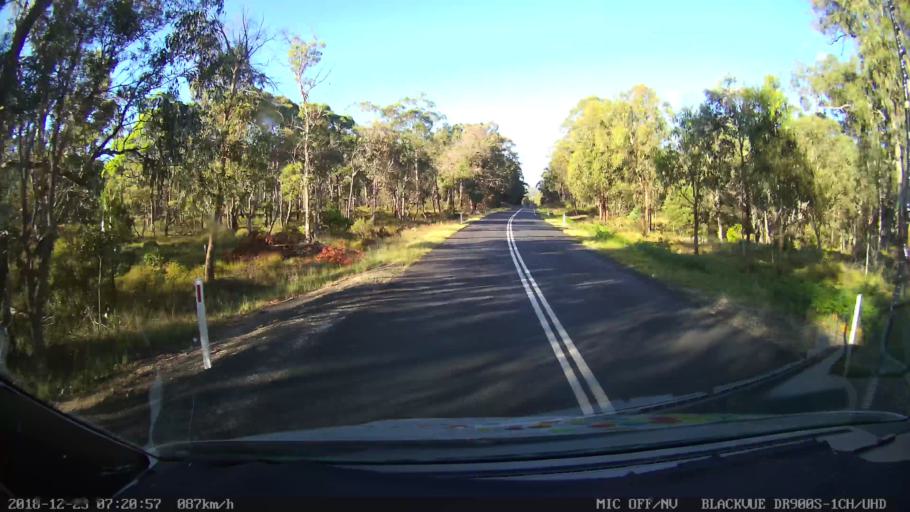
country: AU
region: New South Wales
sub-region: Bellingen
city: Dorrigo
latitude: -30.4946
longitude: 152.2699
